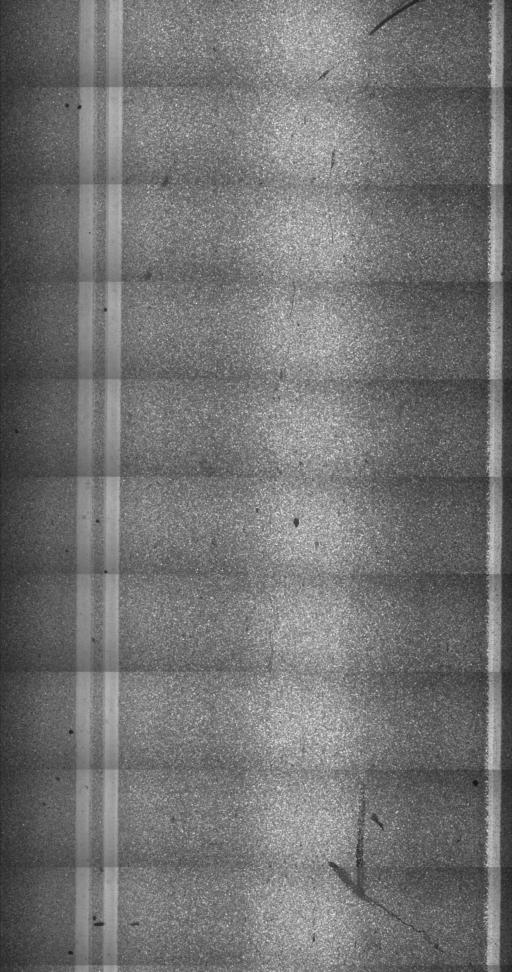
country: US
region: Vermont
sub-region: Bennington County
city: North Bennington
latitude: 42.9120
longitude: -73.2241
